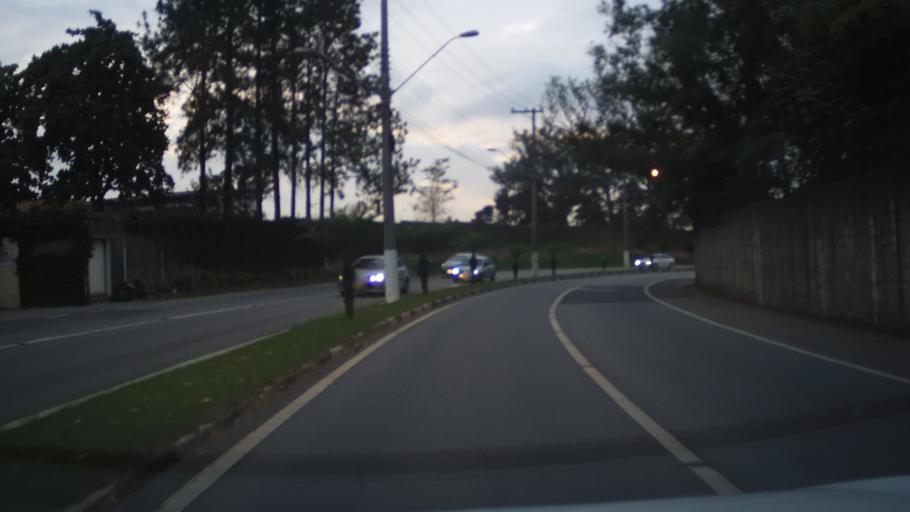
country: BR
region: Sao Paulo
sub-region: Vinhedo
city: Vinhedo
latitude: -23.0368
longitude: -46.9950
